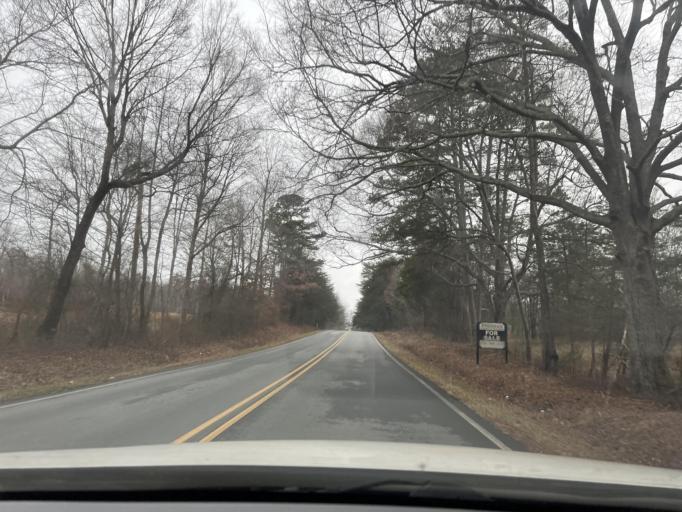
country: US
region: North Carolina
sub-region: Guilford County
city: Pleasant Garden
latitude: 35.9935
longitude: -79.7986
